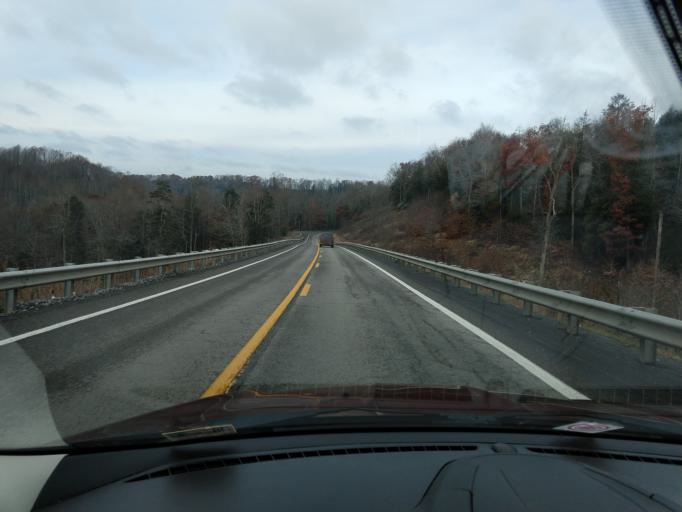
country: US
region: West Virginia
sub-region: Nicholas County
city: Craigsville
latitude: 38.2487
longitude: -80.7221
